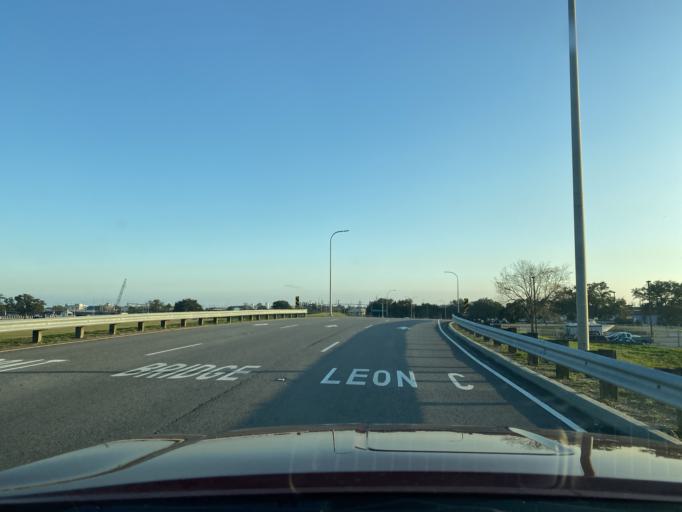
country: US
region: Louisiana
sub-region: Orleans Parish
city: New Orleans
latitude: 30.0340
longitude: -90.0417
